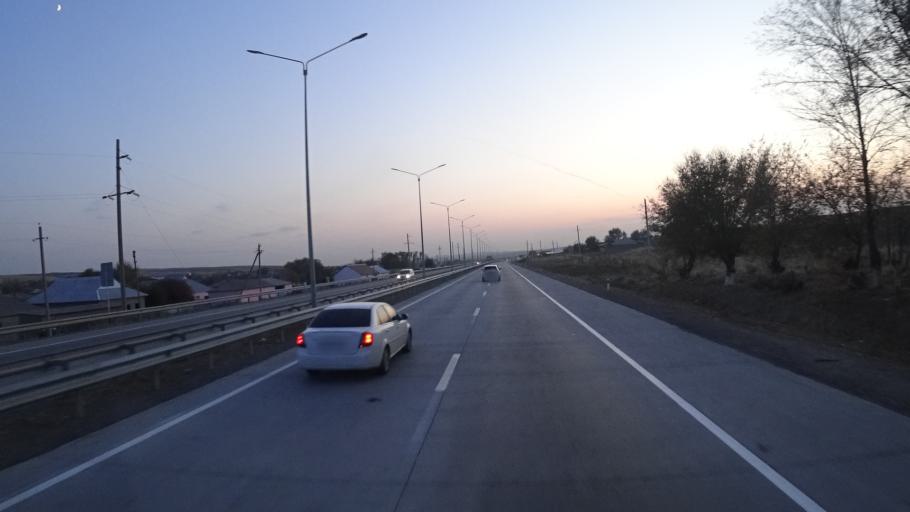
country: KZ
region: Ongtustik Qazaqstan
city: Qazyqurt
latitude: 41.8825
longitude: 69.4386
